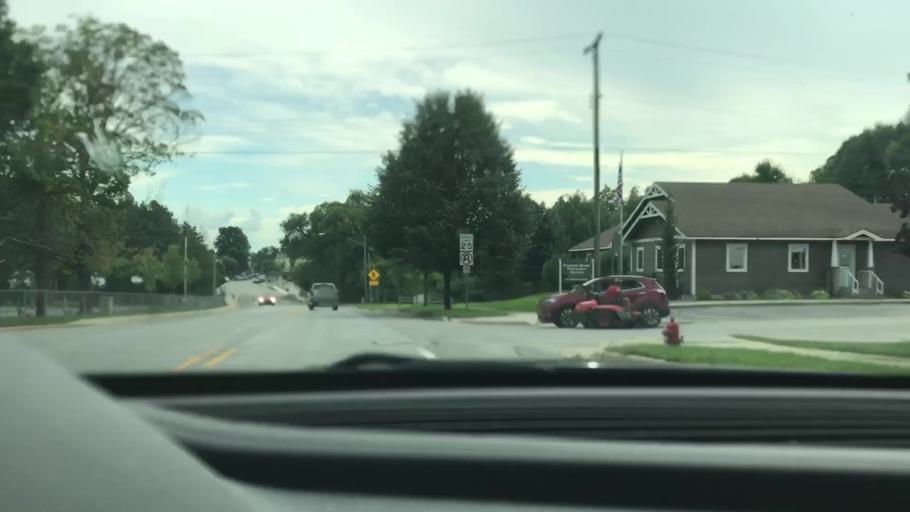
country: US
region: Michigan
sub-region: Antrim County
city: Bellaire
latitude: 44.9802
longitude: -85.2103
